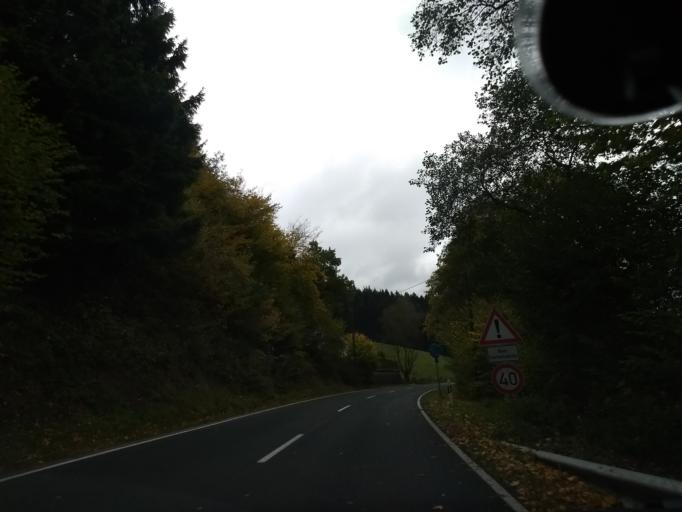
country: DE
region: North Rhine-Westphalia
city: Eslohe
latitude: 51.2416
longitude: 8.0751
